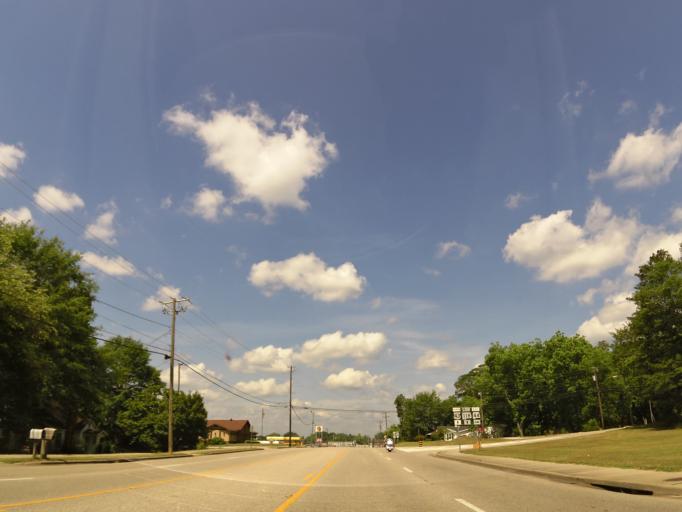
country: US
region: Alabama
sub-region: Marion County
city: Guin
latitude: 33.9662
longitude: -87.9074
